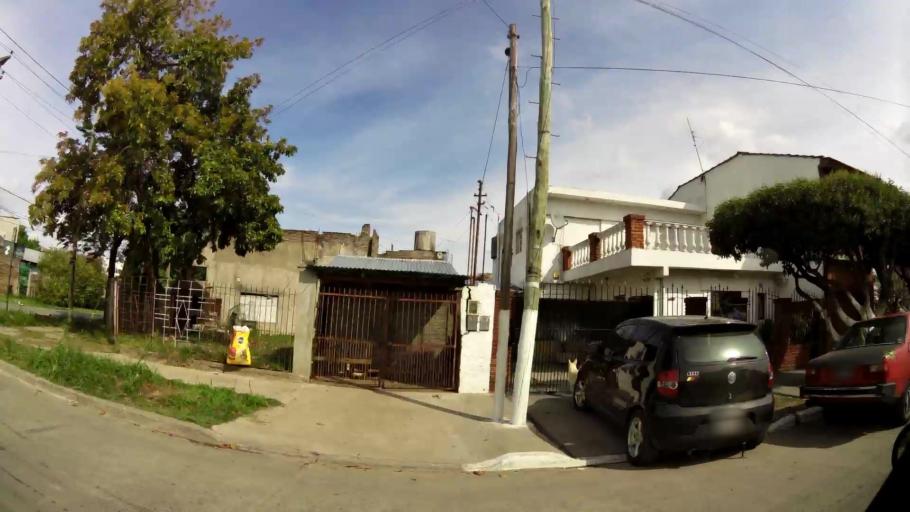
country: AR
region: Buenos Aires
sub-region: Partido de Quilmes
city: Quilmes
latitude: -34.7698
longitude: -58.2505
